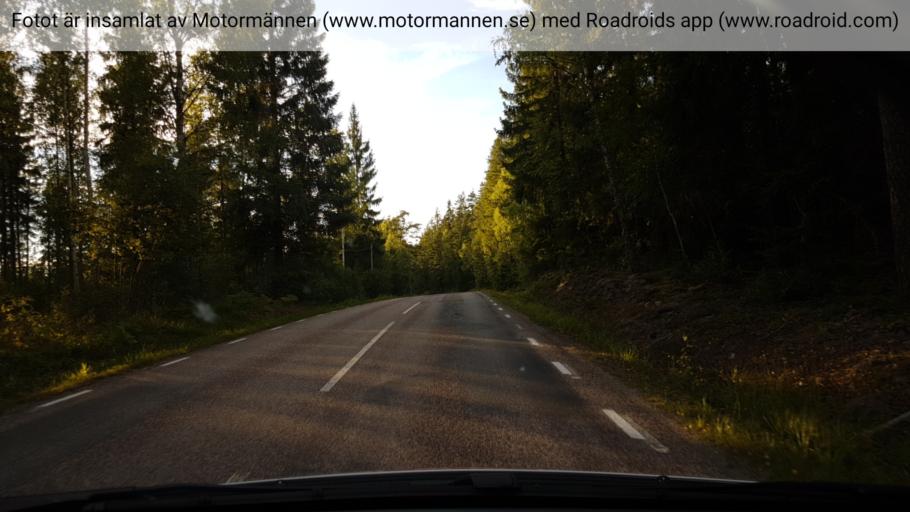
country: SE
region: Vaestmanland
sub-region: Vasteras
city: Skultuna
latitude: 59.7487
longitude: 16.3265
